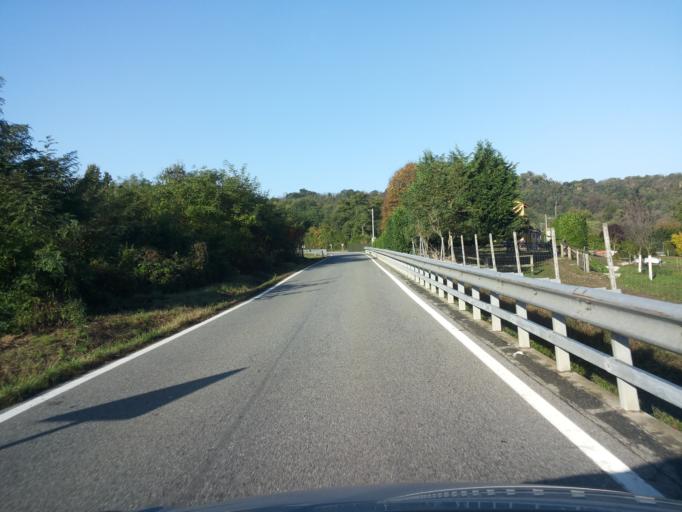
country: IT
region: Piedmont
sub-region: Provincia di Torino
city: Tonengo-Casale
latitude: 45.3006
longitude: 7.9529
